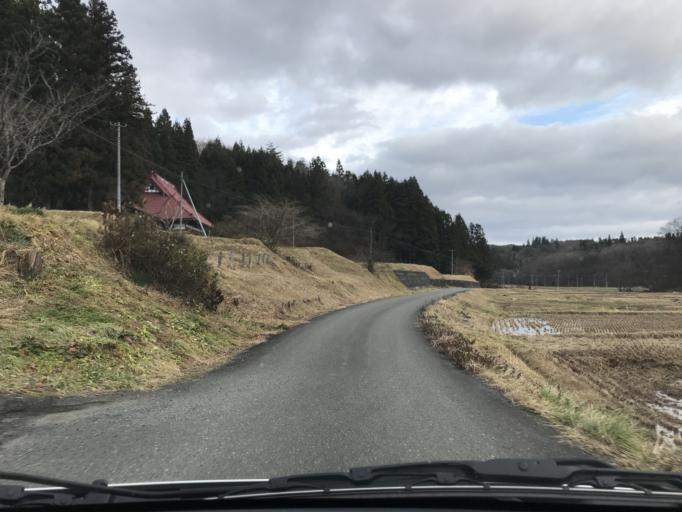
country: JP
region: Iwate
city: Ichinoseki
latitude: 38.9716
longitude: 141.0582
